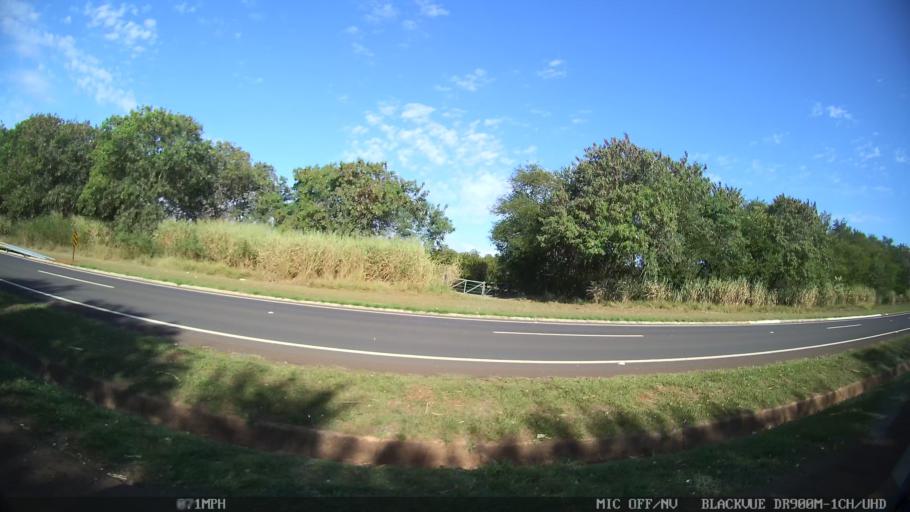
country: BR
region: Sao Paulo
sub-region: Iracemapolis
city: Iracemapolis
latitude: -22.6620
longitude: -47.5298
